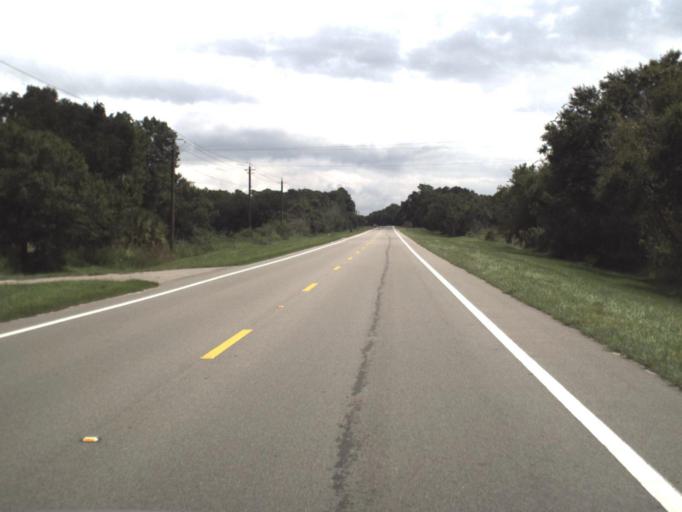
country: US
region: Florida
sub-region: Manatee County
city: Ellenton
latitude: 27.5877
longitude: -82.4165
